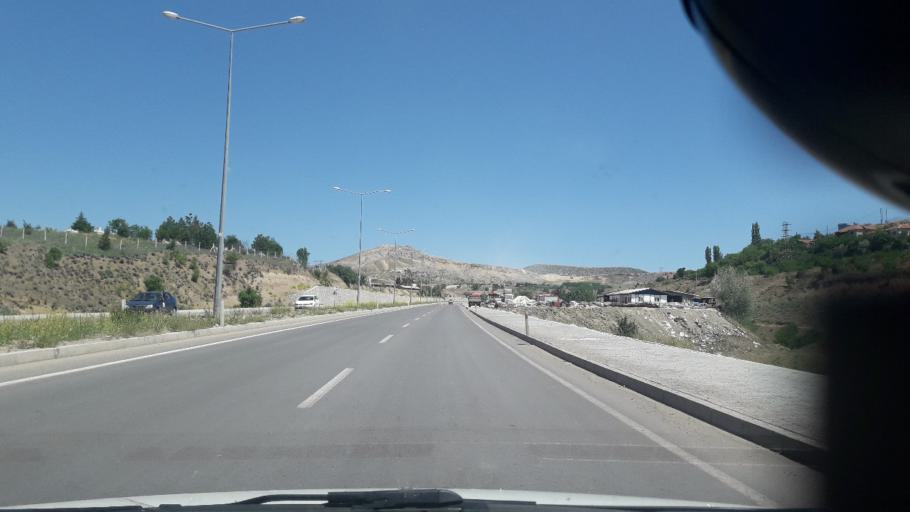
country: TR
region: Malatya
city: Hekimhan
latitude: 38.8189
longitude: 37.9367
